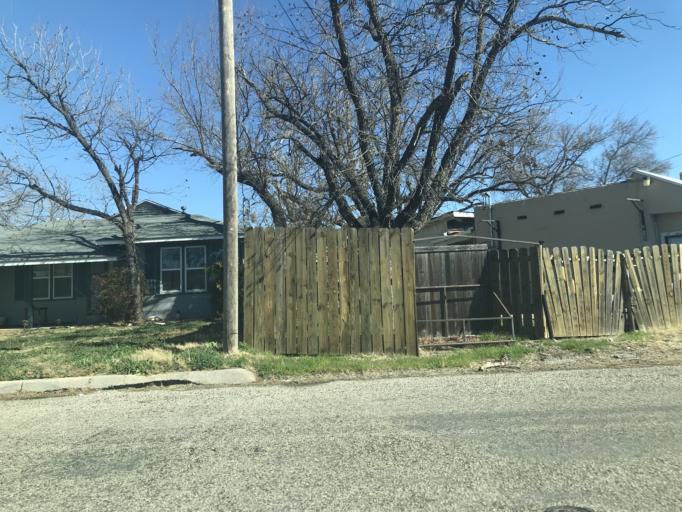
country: US
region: Texas
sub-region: Tom Green County
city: San Angelo
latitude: 31.4434
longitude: -100.4586
